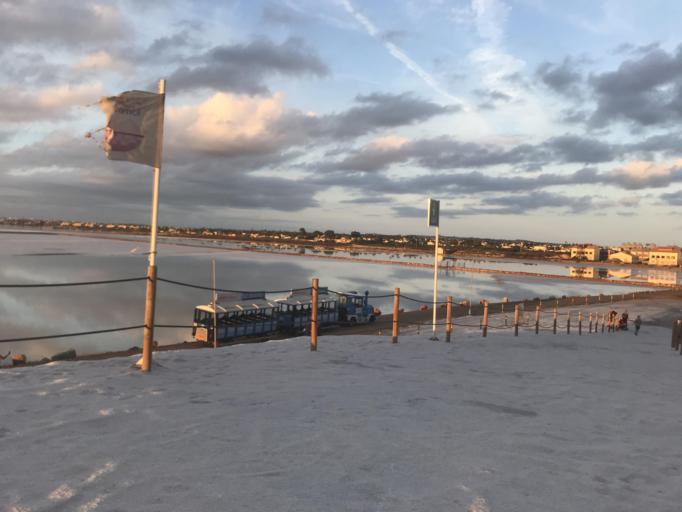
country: ES
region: Valencia
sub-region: Provincia de Alicante
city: Torrevieja
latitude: 37.9802
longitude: -0.7064
